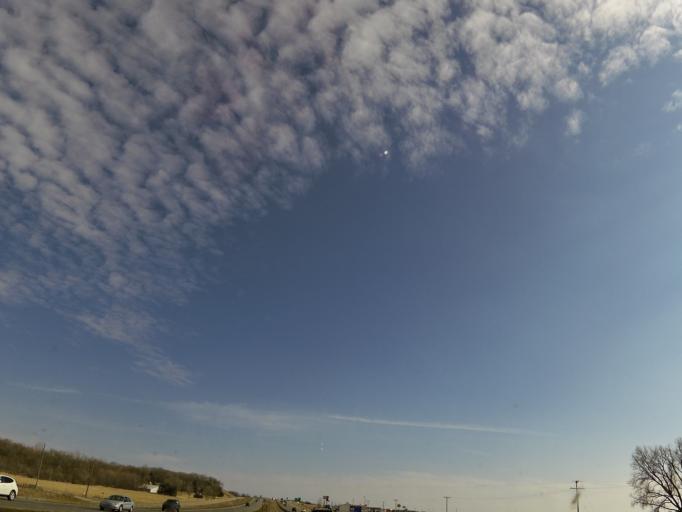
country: US
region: Minnesota
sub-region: Steele County
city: Medford
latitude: 44.1471
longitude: -93.2563
